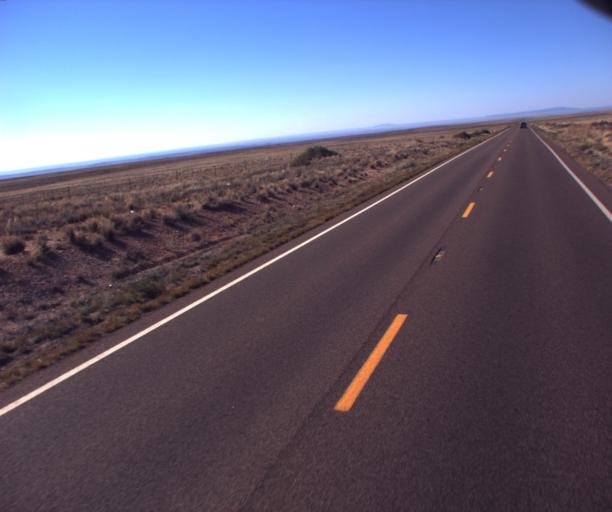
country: US
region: Arizona
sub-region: Navajo County
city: Joseph City
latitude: 35.1423
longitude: -110.4818
